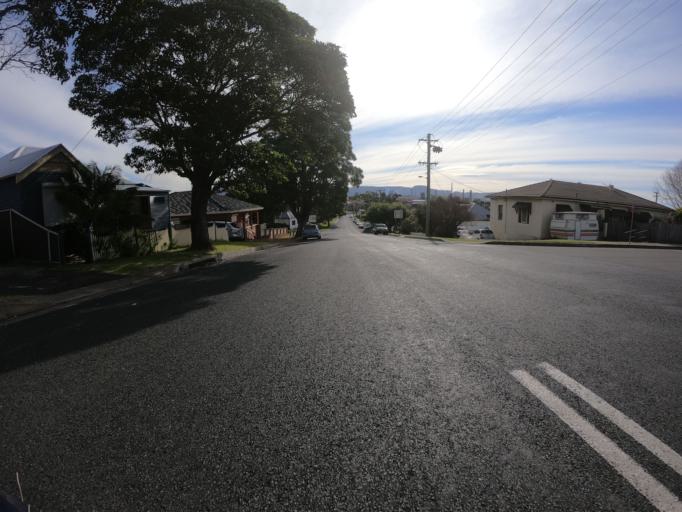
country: AU
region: New South Wales
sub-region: Wollongong
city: Port Kembla
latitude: -34.4835
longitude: 150.9024
